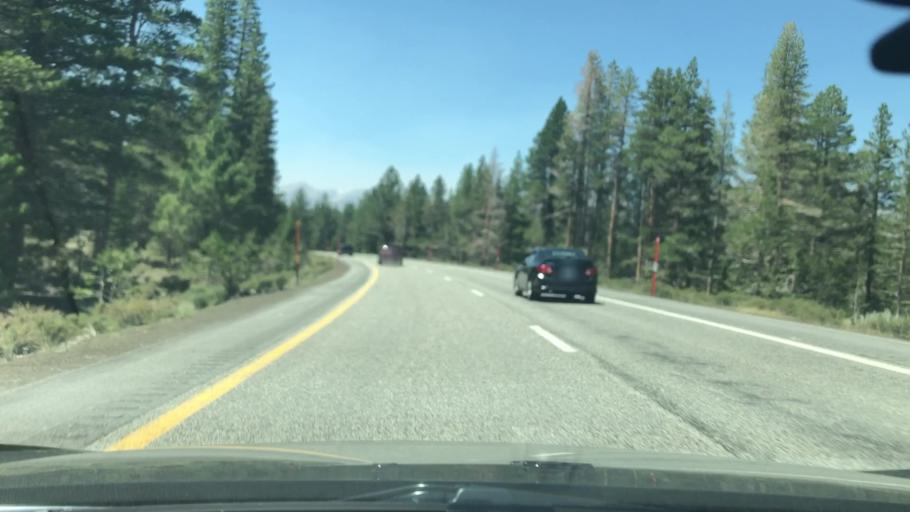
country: US
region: California
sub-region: Mono County
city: Mammoth Lakes
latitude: 37.7875
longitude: -119.0239
